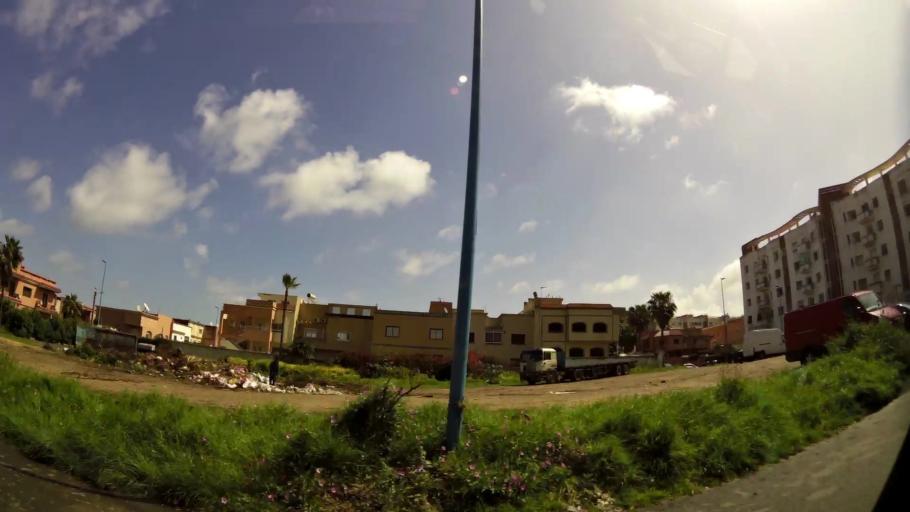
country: MA
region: Grand Casablanca
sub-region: Mediouna
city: Tit Mellil
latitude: 33.6143
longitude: -7.5291
